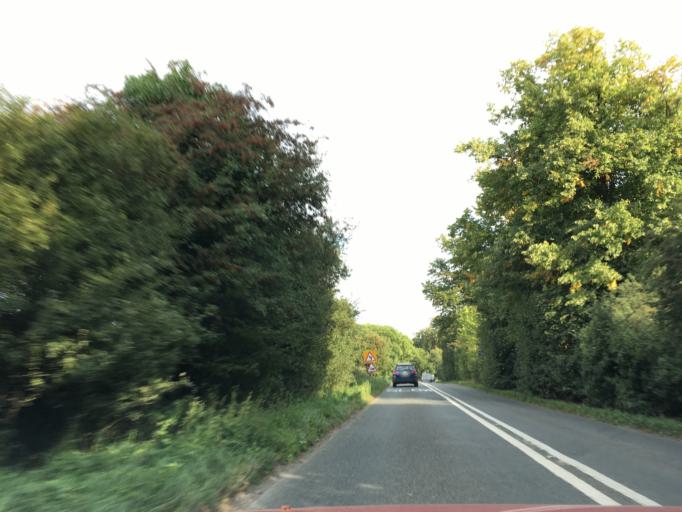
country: GB
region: England
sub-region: Gloucestershire
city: Tetbury
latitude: 51.6392
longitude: -2.1779
